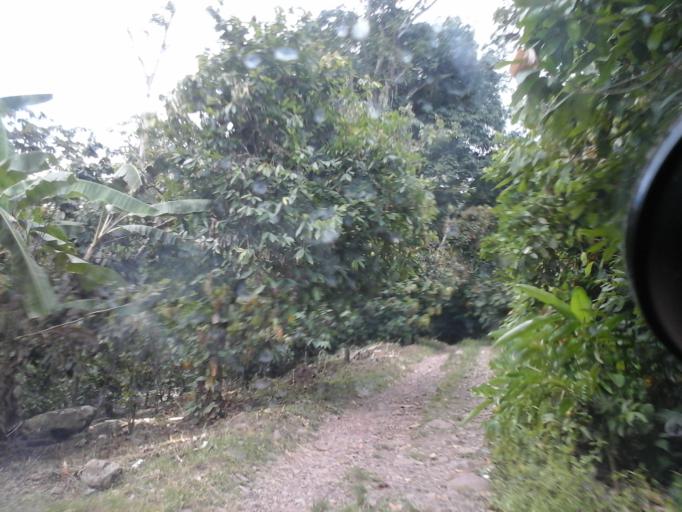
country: CO
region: Cesar
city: San Diego
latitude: 10.2891
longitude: -73.0818
